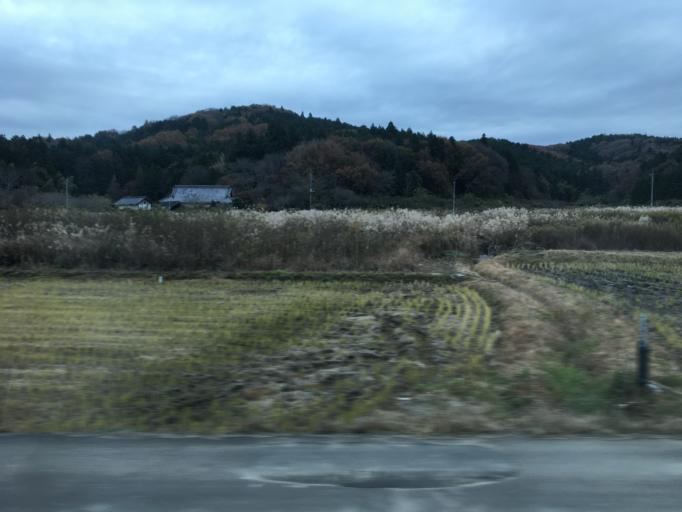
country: JP
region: Ibaraki
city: Kasama
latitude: 36.3729
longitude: 140.2227
